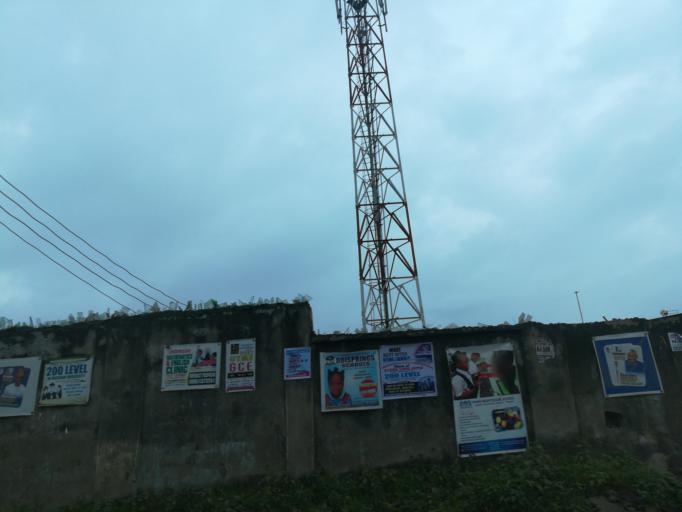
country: NG
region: Lagos
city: Oshodi
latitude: 6.5663
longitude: 3.3430
